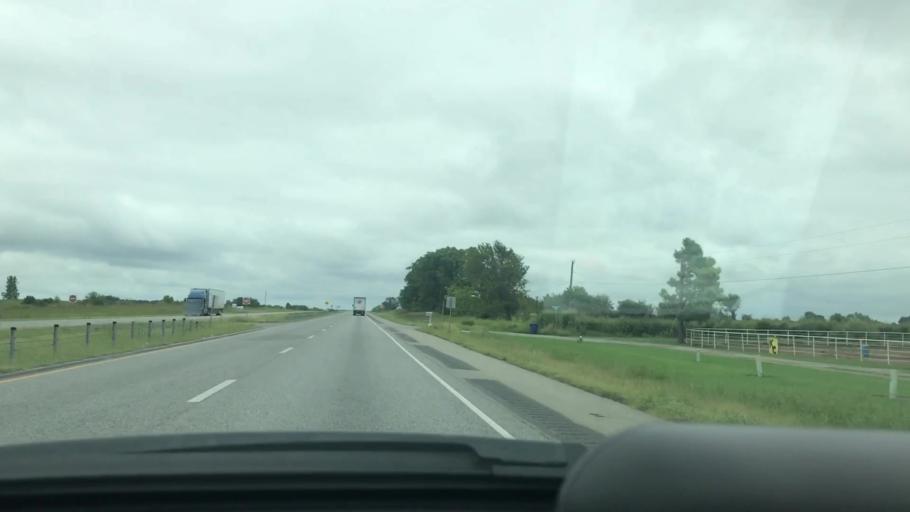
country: US
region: Oklahoma
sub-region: Pittsburg County
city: McAlester
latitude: 34.7489
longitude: -95.8948
